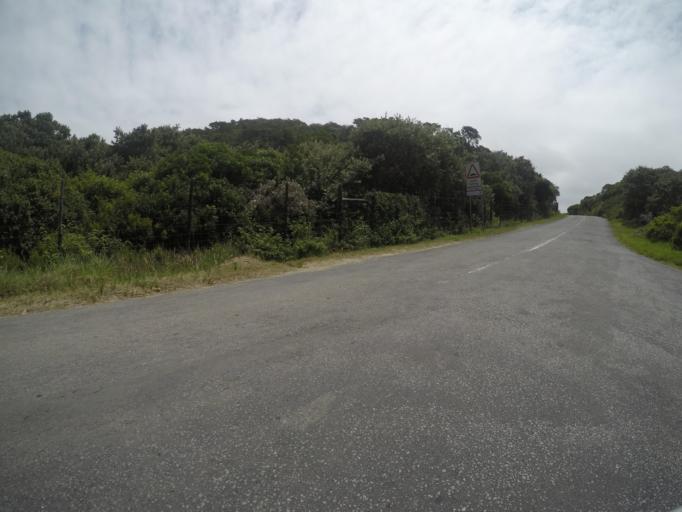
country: ZA
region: Eastern Cape
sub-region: Buffalo City Metropolitan Municipality
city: East London
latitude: -32.9953
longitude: 27.9471
